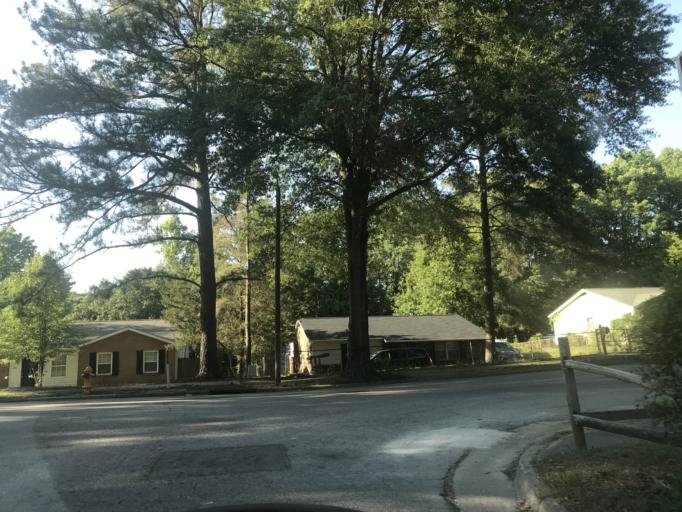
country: US
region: North Carolina
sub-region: Wake County
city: Garner
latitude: 35.7417
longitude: -78.6160
